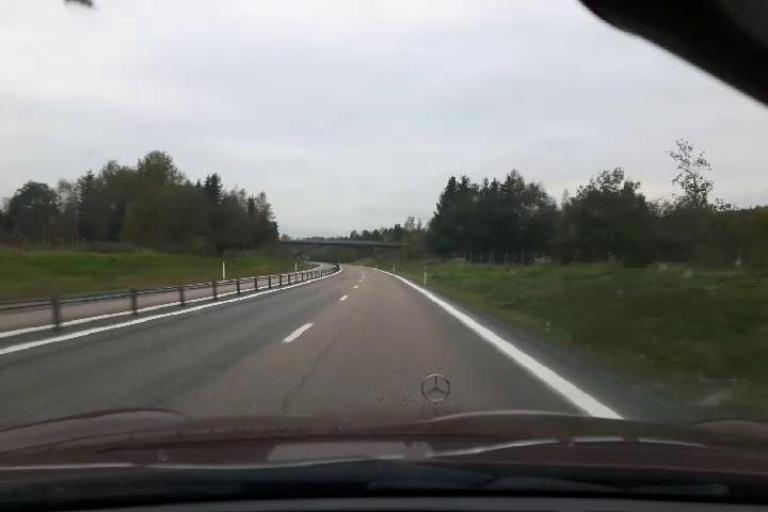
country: SE
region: Vaesternorrland
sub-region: Haernoesands Kommun
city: Haernoesand
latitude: 62.8704
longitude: 18.0419
